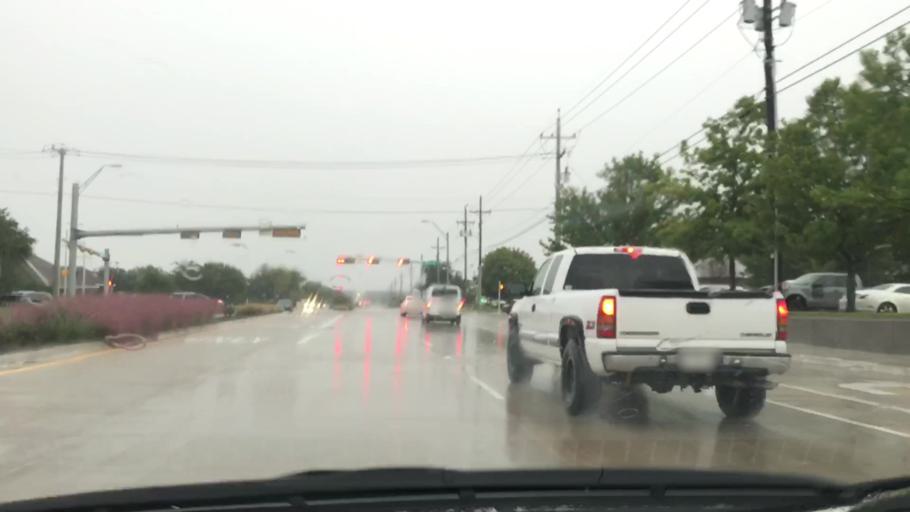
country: US
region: Texas
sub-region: Rockwall County
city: Rockwall
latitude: 32.8898
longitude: -96.4691
